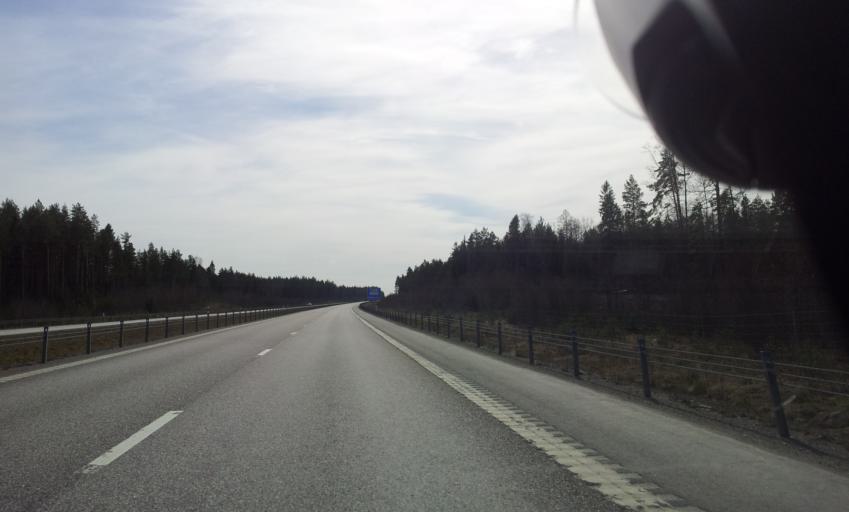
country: SE
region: Uppsala
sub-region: Tierps Kommun
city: Tierp
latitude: 60.2354
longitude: 17.5013
